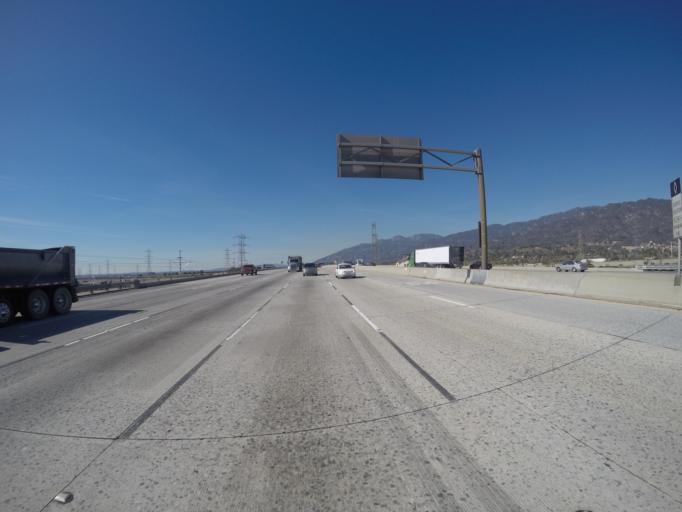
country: US
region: California
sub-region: Los Angeles County
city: Bradbury
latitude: 34.1316
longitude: -117.9484
